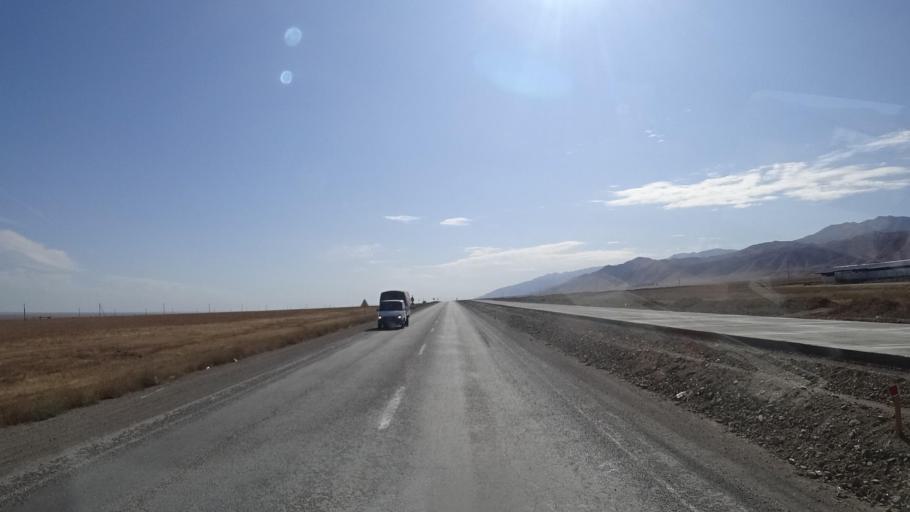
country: KG
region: Chuy
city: Ivanovka
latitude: 43.3902
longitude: 75.1426
